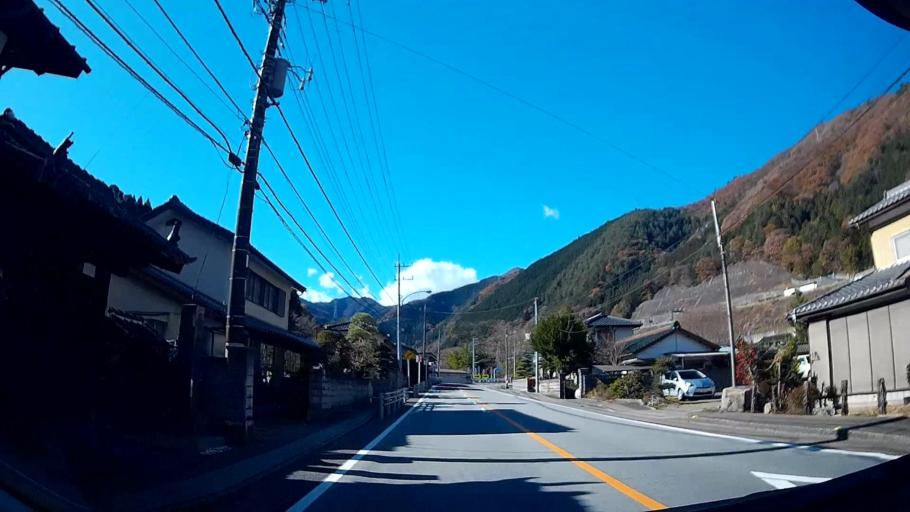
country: JP
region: Yamanashi
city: Otsuki
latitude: 35.6047
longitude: 138.8203
